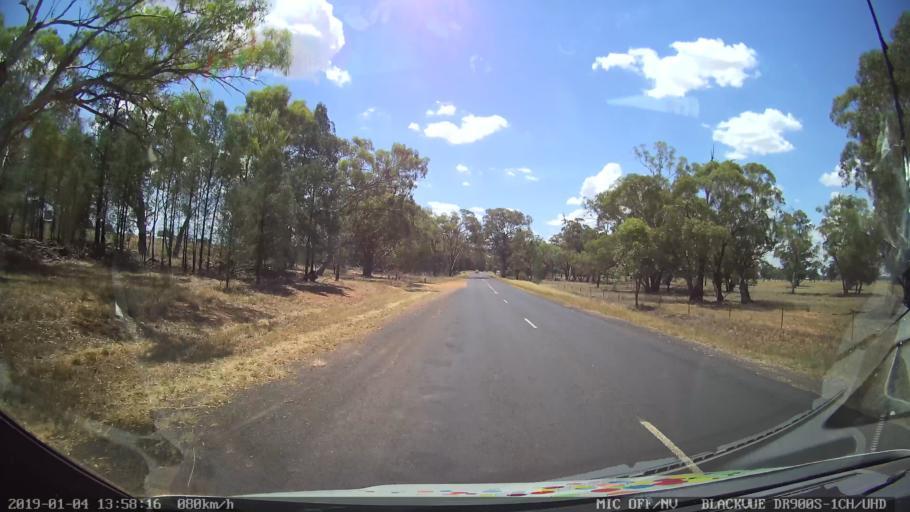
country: AU
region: New South Wales
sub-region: Dubbo Municipality
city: Dubbo
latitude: -32.3306
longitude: 148.5947
